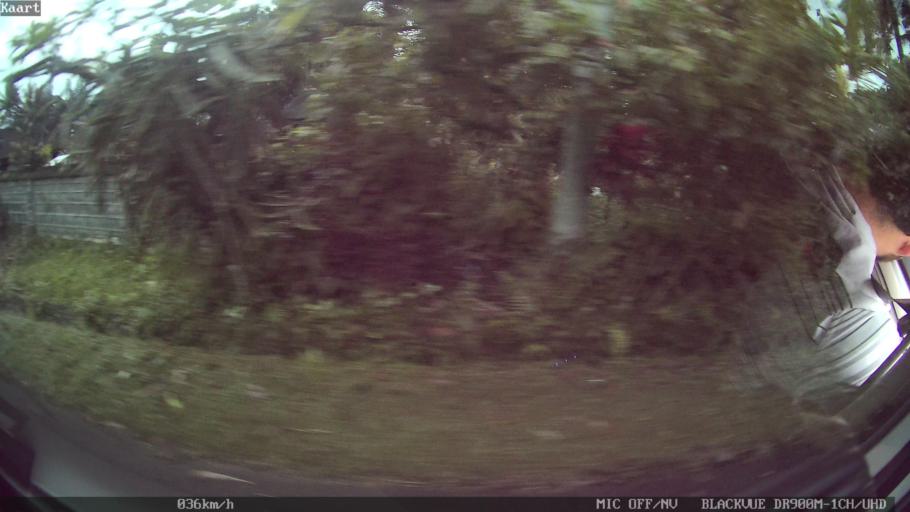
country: ID
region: Bali
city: Petang
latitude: -8.4126
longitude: 115.2238
